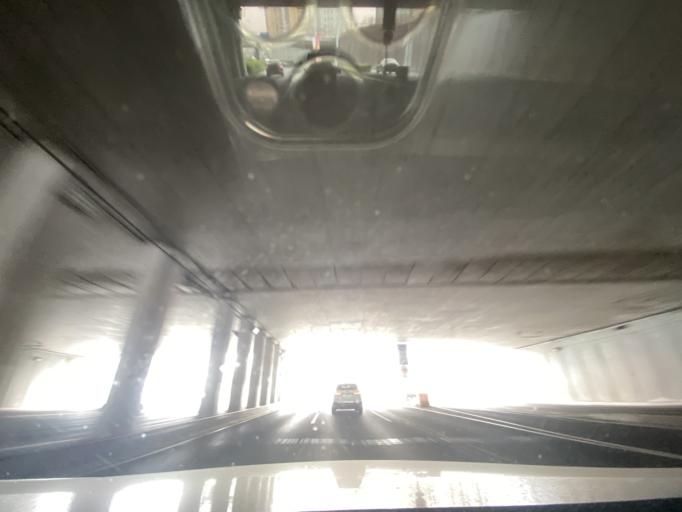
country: CN
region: Beijing
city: Jinrongjie
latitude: 39.9372
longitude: 116.3379
